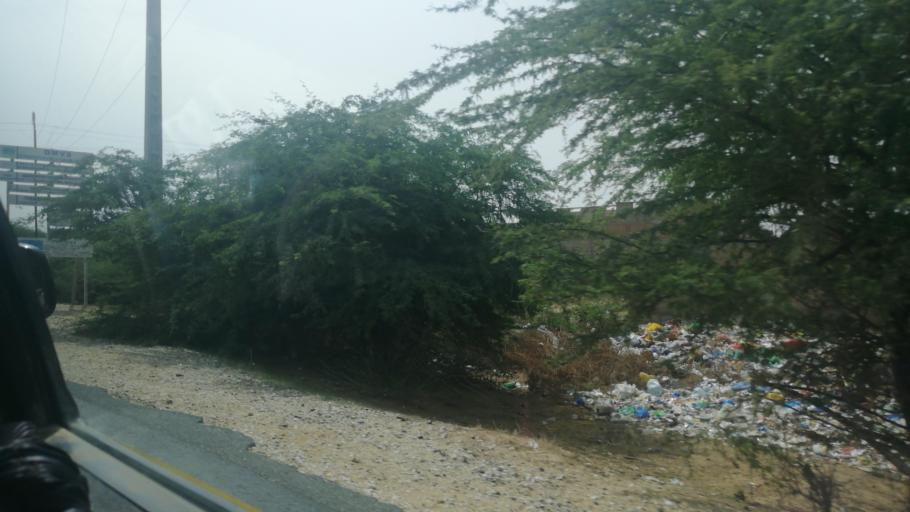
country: SN
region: Saint-Louis
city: Saint-Louis
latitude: 16.0719
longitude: -16.3886
